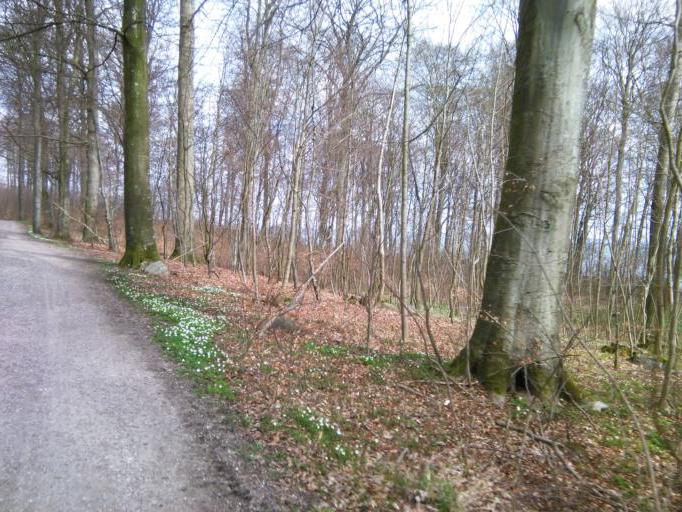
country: DK
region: Central Jutland
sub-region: Arhus Kommune
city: Beder
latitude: 56.0793
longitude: 10.2513
